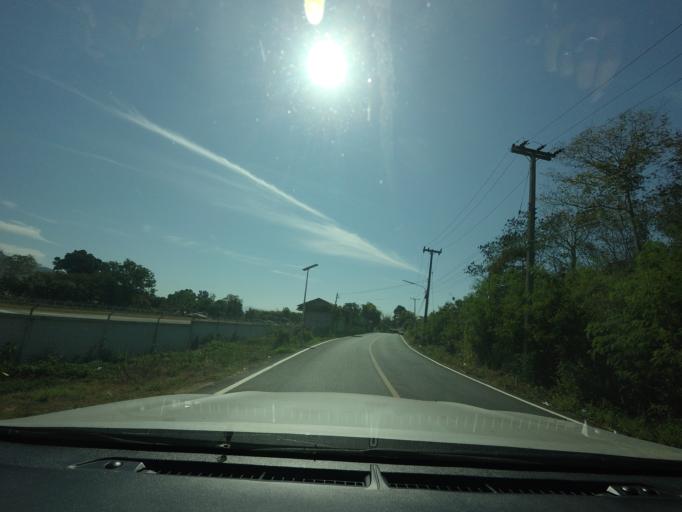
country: TH
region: Chiang Mai
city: Pai
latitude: 19.3699
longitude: 98.4347
